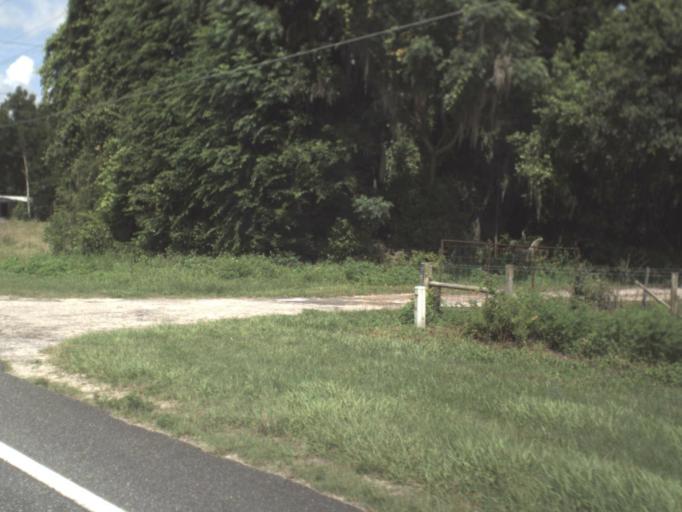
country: US
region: Florida
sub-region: Alachua County
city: Archer
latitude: 29.5498
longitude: -82.4978
